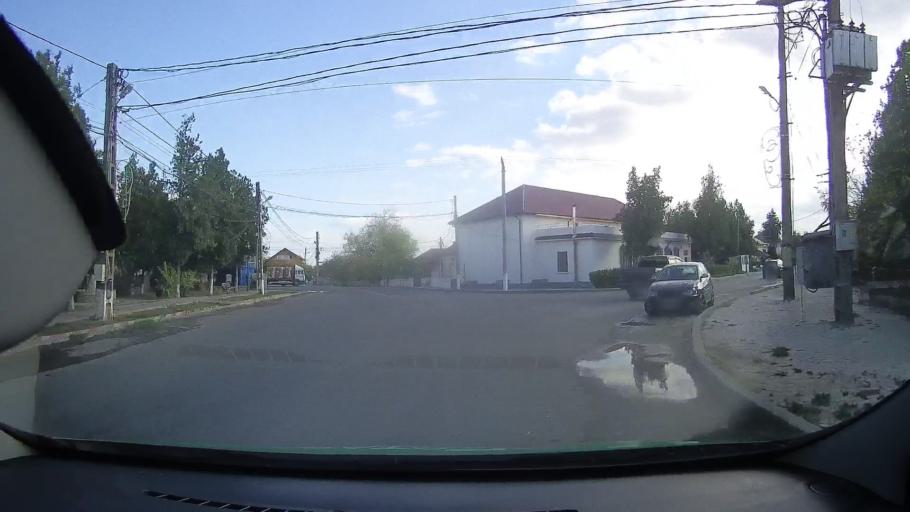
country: RO
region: Constanta
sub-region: Comuna Sacele
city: Sacele
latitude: 44.4873
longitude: 28.6442
